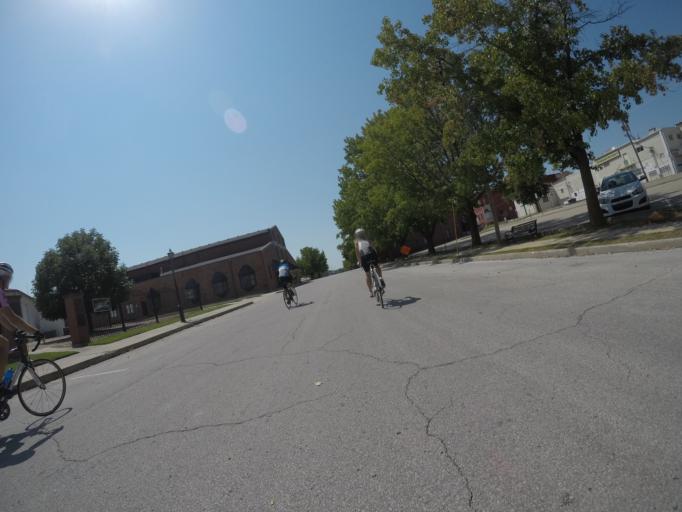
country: US
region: Kansas
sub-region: Leavenworth County
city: Leavenworth
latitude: 39.3178
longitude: -94.9095
